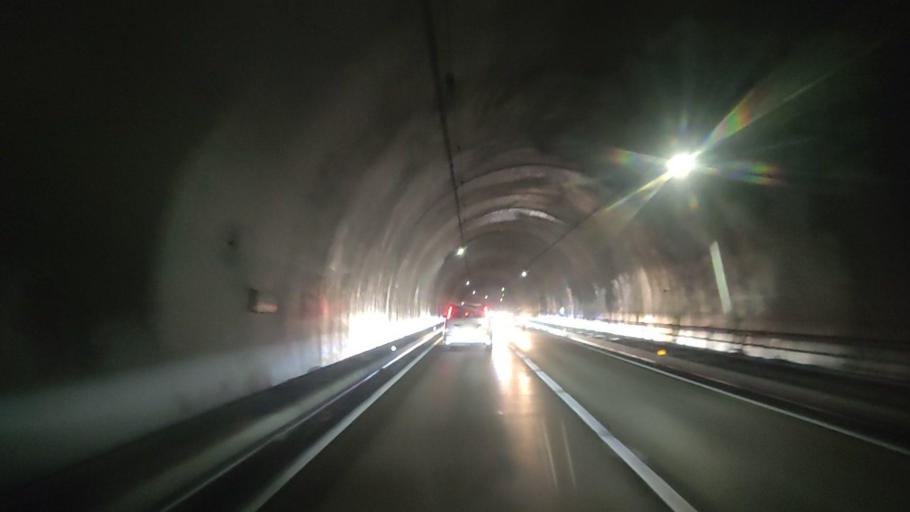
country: JP
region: Gifu
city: Godo
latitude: 35.5132
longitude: 136.6590
